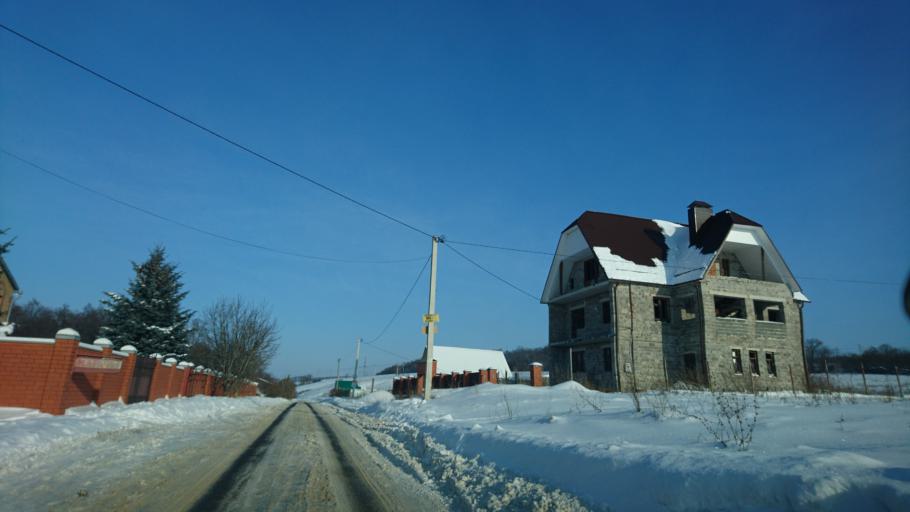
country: RU
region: Belgorod
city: Severnyy
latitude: 50.7243
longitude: 36.6110
